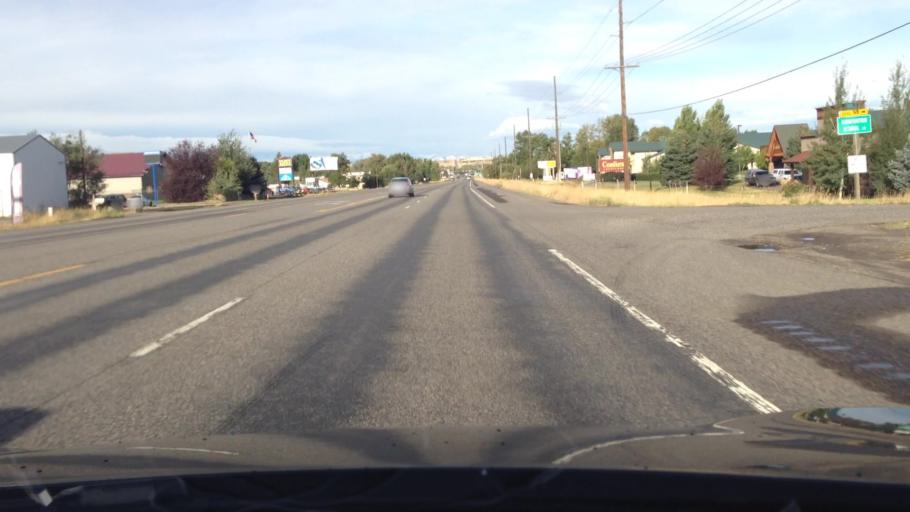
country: US
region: Montana
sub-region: Gallatin County
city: Four Corners
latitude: 45.6710
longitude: -111.1695
